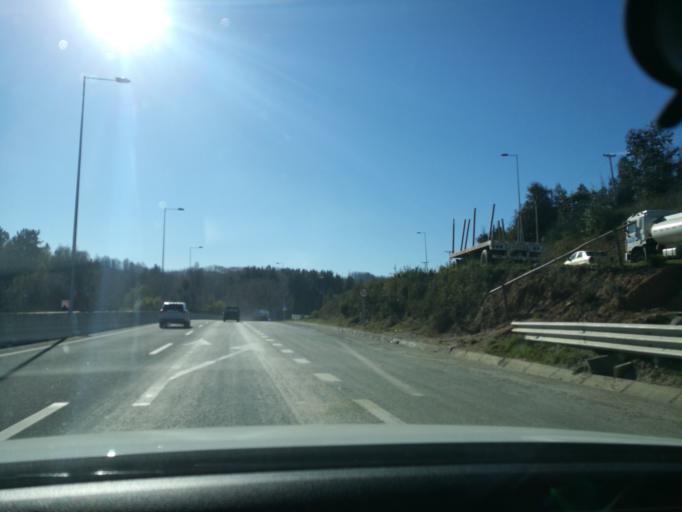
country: CL
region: Biobio
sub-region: Provincia de Concepcion
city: Penco
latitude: -36.8566
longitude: -72.8803
